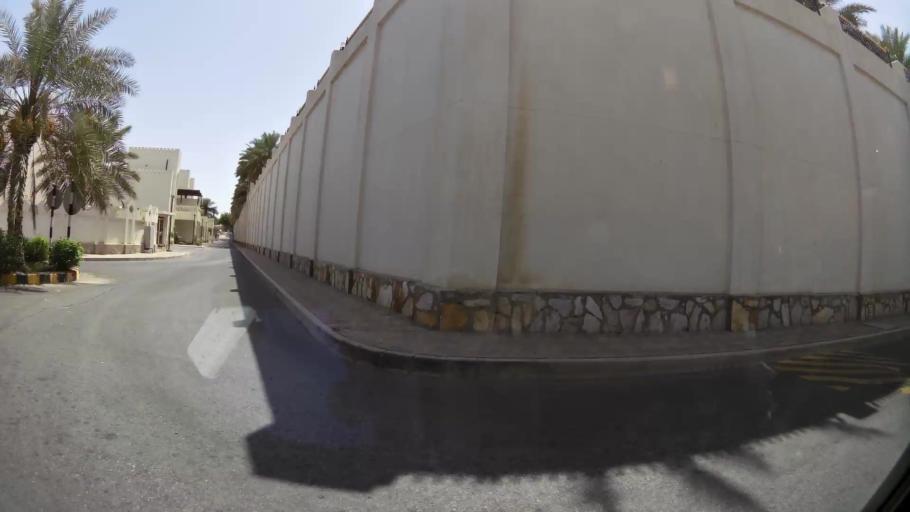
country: OM
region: Muhafazat Masqat
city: Bawshar
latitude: 23.5960
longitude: 58.4511
